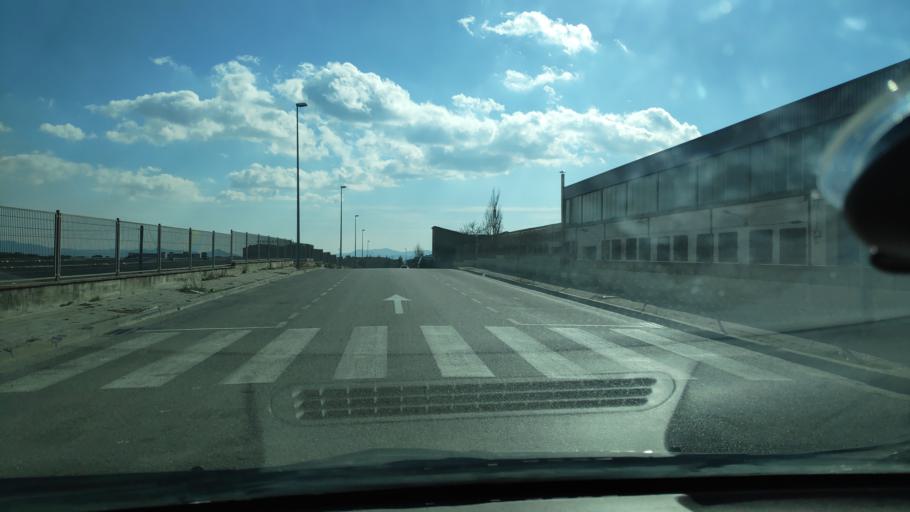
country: ES
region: Catalonia
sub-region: Provincia de Barcelona
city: Sant Quirze del Valles
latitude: 41.5410
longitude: 2.0765
